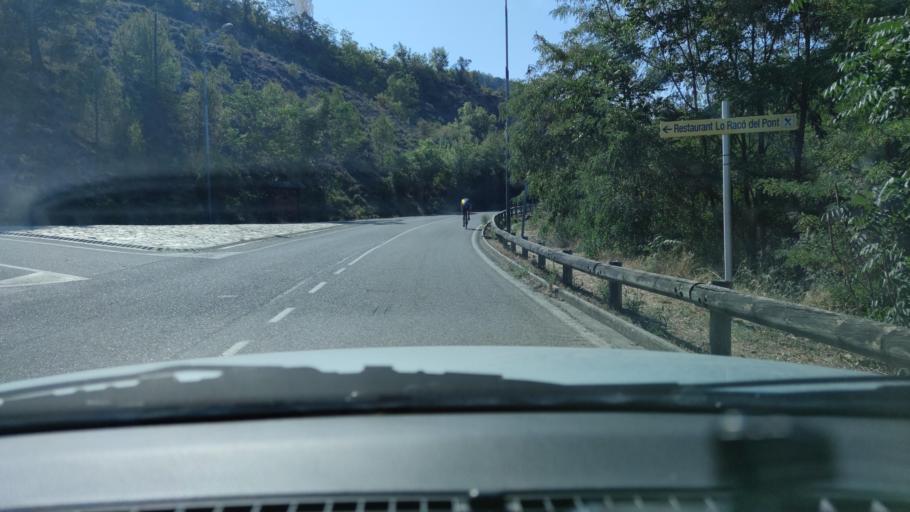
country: ES
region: Catalonia
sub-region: Provincia de Lleida
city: Senterada
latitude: 42.2425
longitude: 0.9713
